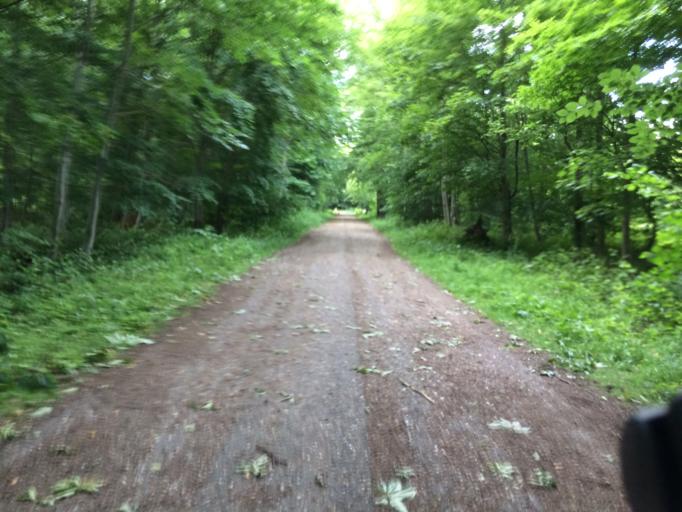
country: FR
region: Ile-de-France
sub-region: Departement des Hauts-de-Seine
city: Chatenay-Malabry
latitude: 48.7614
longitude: 2.2465
